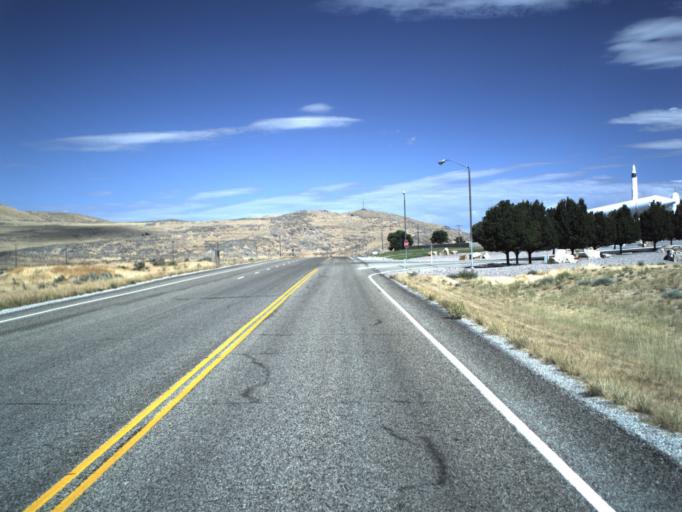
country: US
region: Utah
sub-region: Box Elder County
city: Tremonton
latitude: 41.6570
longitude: -112.4409
